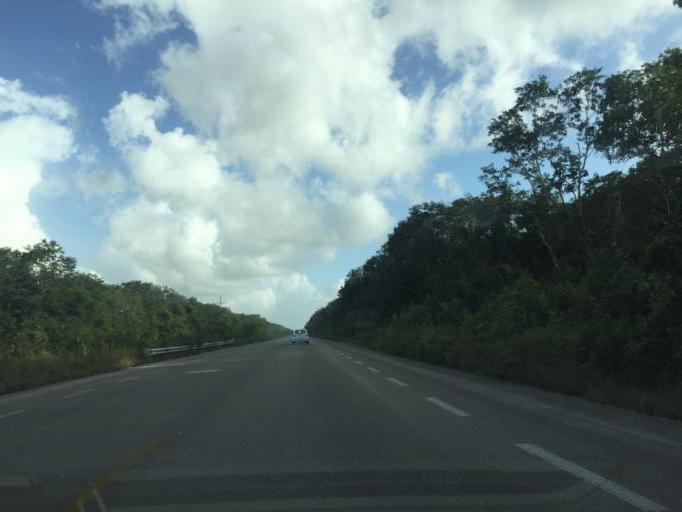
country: MX
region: Quintana Roo
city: Coba
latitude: 20.4604
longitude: -87.6781
